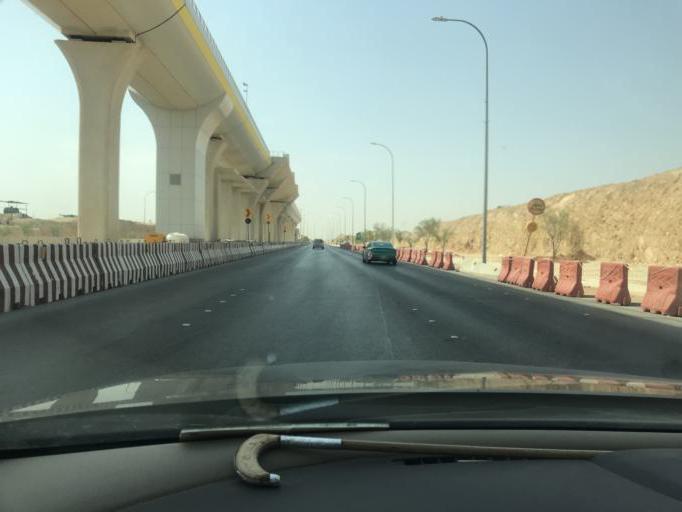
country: SA
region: Ar Riyad
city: Riyadh
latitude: 24.8794
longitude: 46.6945
